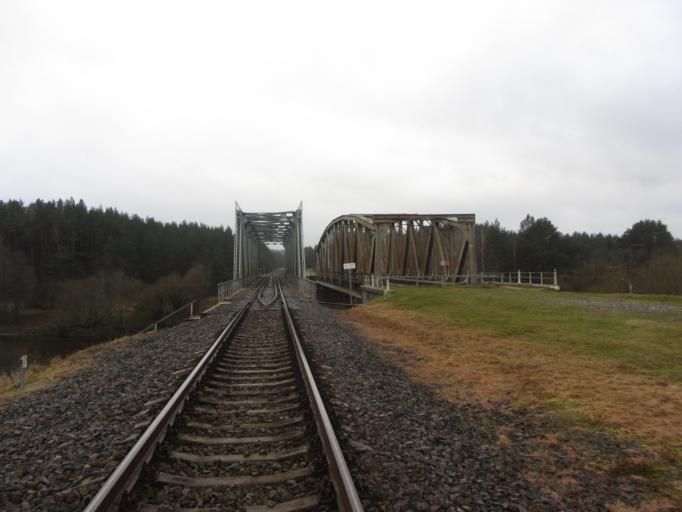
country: LT
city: Nemencine
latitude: 54.9006
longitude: 25.6437
